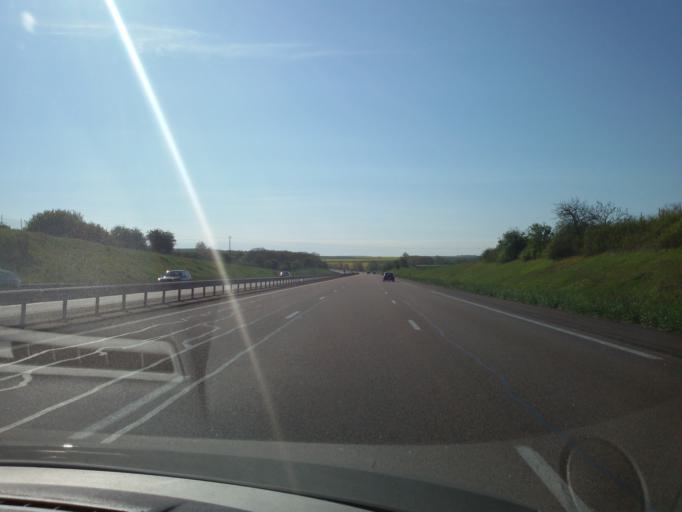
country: FR
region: Bourgogne
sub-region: Departement de l'Yonne
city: Aillant-sur-Tholon
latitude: 47.9063
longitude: 3.3416
